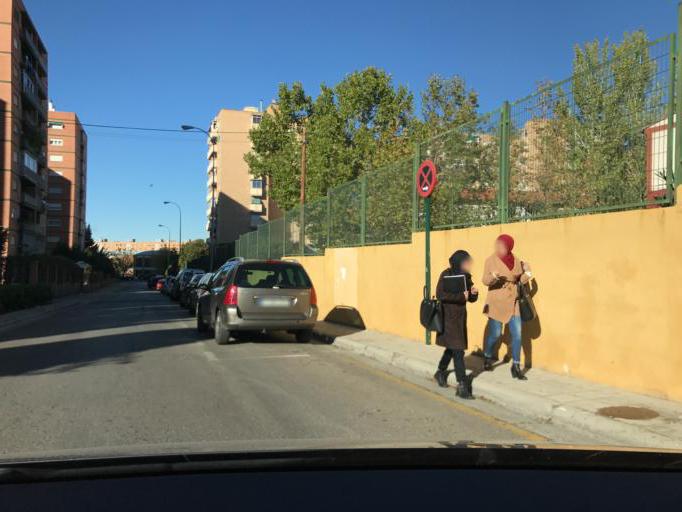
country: ES
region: Andalusia
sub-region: Provincia de Granada
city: Granada
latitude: 37.2037
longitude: -3.5986
